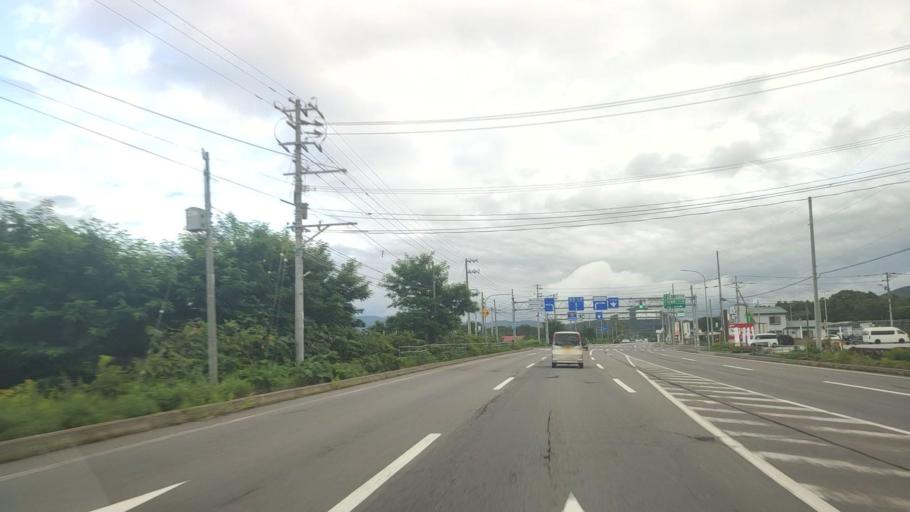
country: JP
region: Hokkaido
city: Nanae
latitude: 42.0083
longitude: 140.6311
